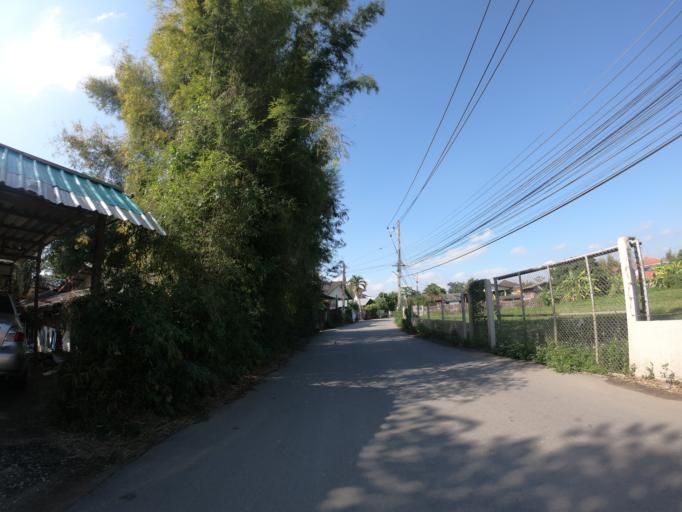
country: TH
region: Chiang Mai
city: Saraphi
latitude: 18.7134
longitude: 99.0047
